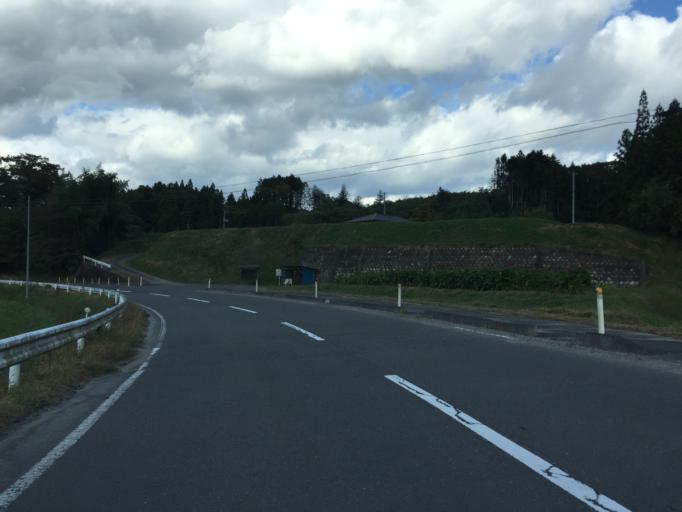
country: JP
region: Miyagi
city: Marumori
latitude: 37.8506
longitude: 140.8321
